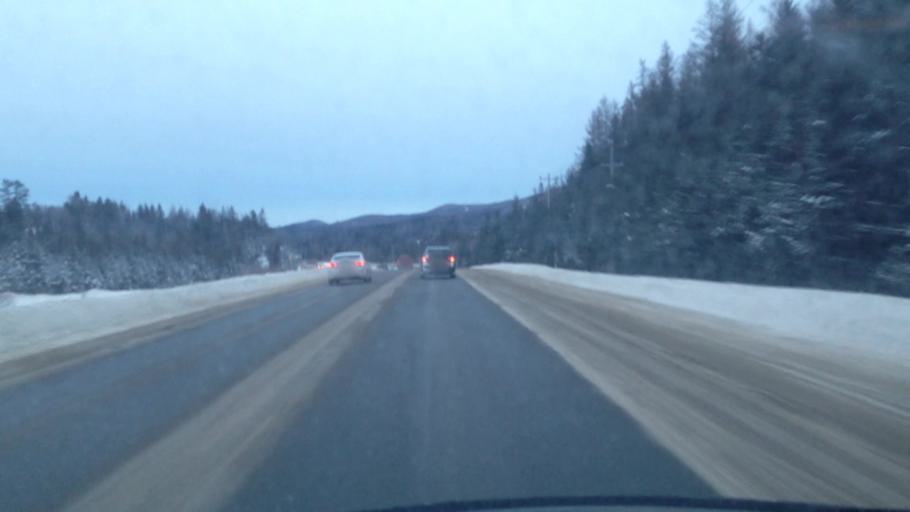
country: CA
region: Quebec
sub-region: Laurentides
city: Mont-Tremblant
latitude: 46.1123
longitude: -74.5349
